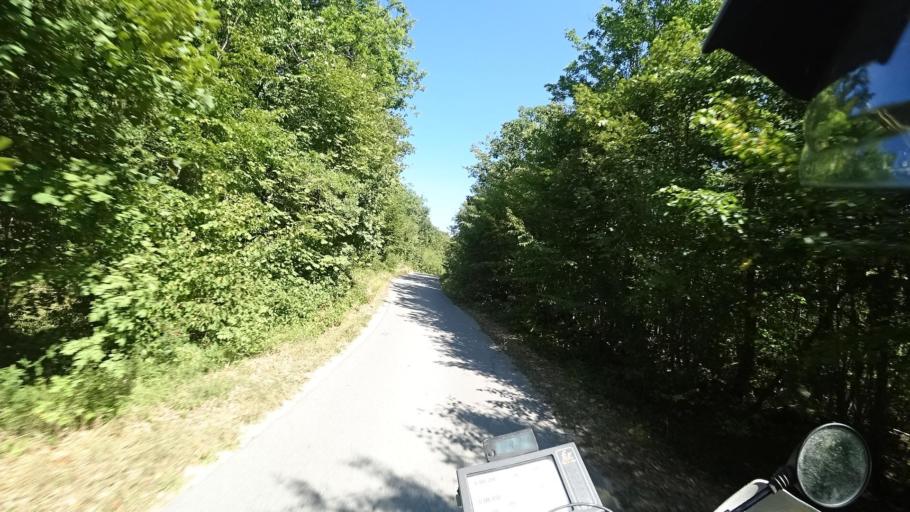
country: HR
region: Licko-Senjska
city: Otocac
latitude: 44.7429
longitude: 15.3720
